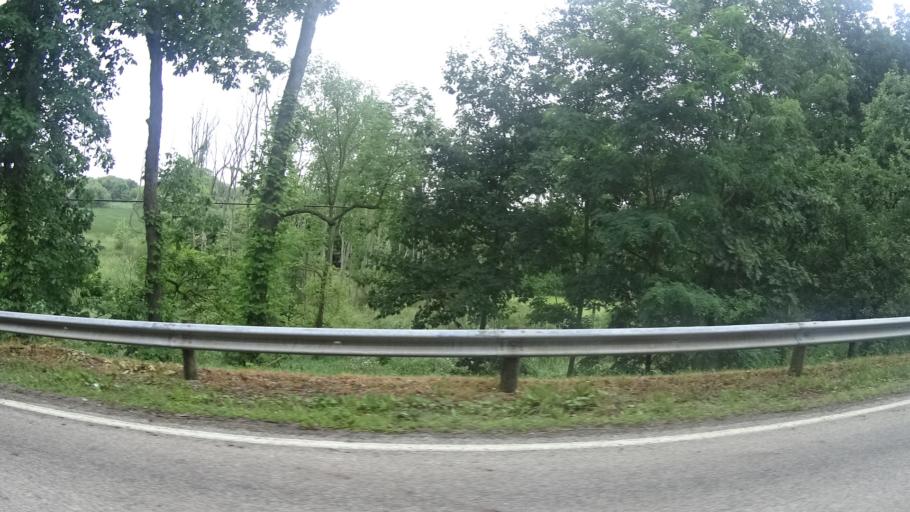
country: US
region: Ohio
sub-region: Erie County
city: Huron
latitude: 41.3522
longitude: -82.5506
